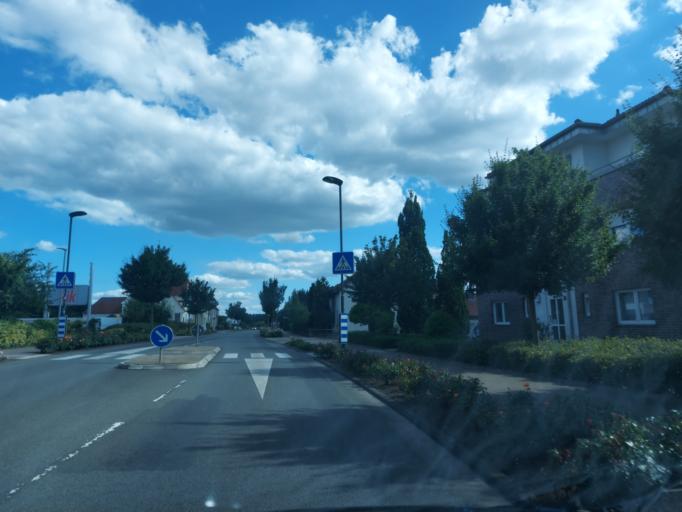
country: DE
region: Lower Saxony
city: Hilter
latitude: 52.1340
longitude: 8.1506
